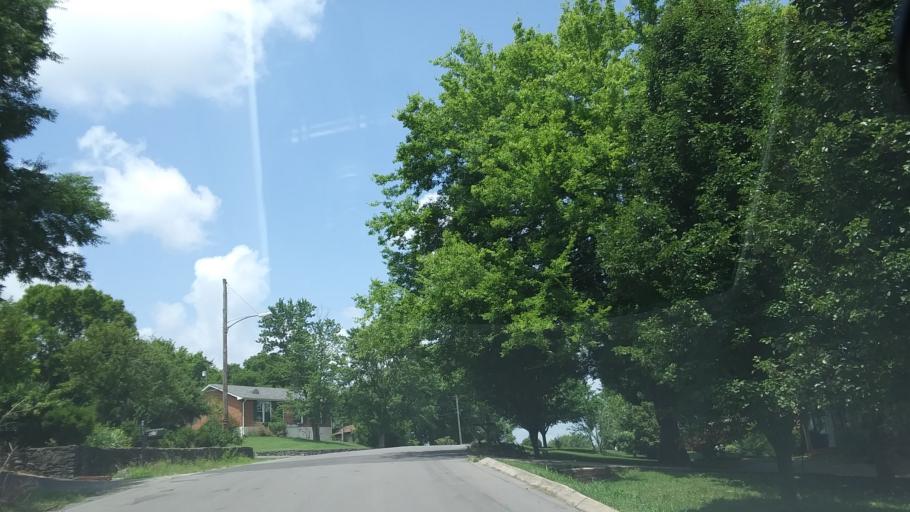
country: US
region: Tennessee
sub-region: Davidson County
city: Belle Meade
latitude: 36.1455
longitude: -86.8744
